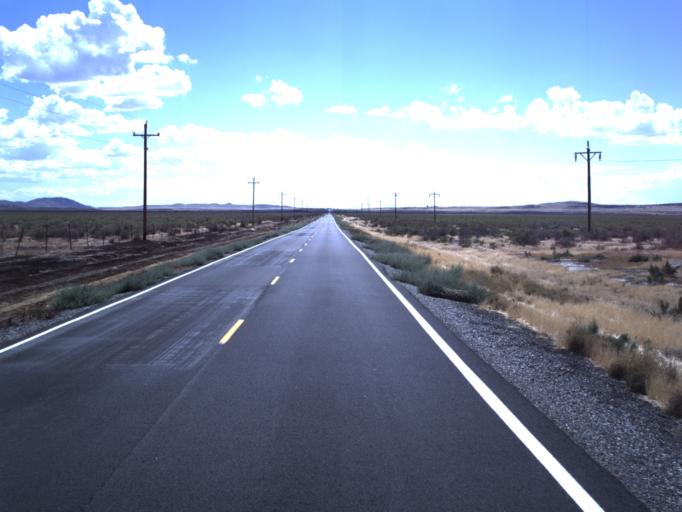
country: US
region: Utah
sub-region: Tooele County
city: Grantsville
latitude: 40.2797
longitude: -112.6715
